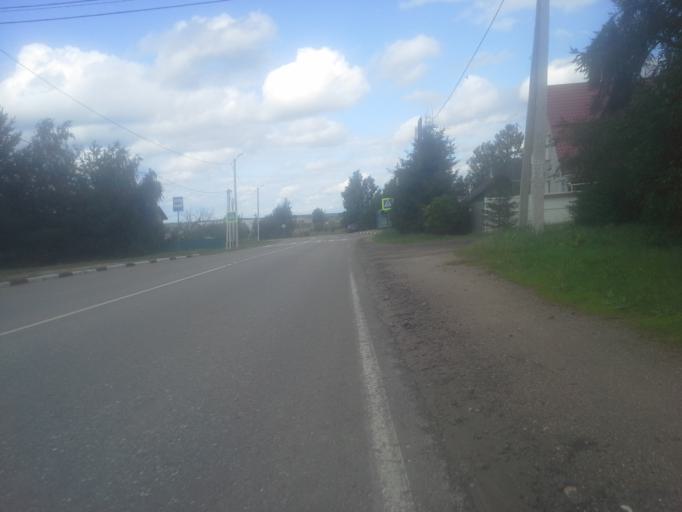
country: RU
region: Moskovskaya
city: Karinskoye
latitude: 55.6836
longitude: 36.6682
